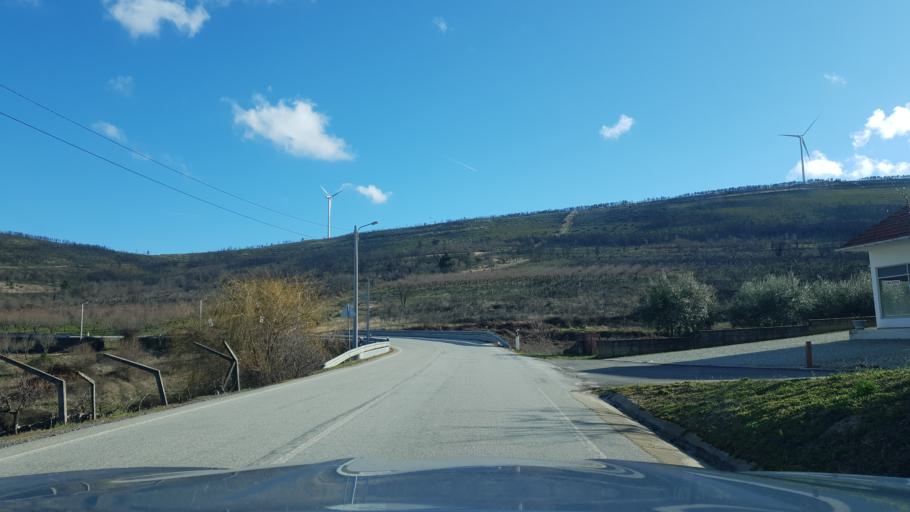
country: PT
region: Braganca
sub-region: Torre de Moncorvo
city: Torre de Moncorvo
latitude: 41.1821
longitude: -6.9772
